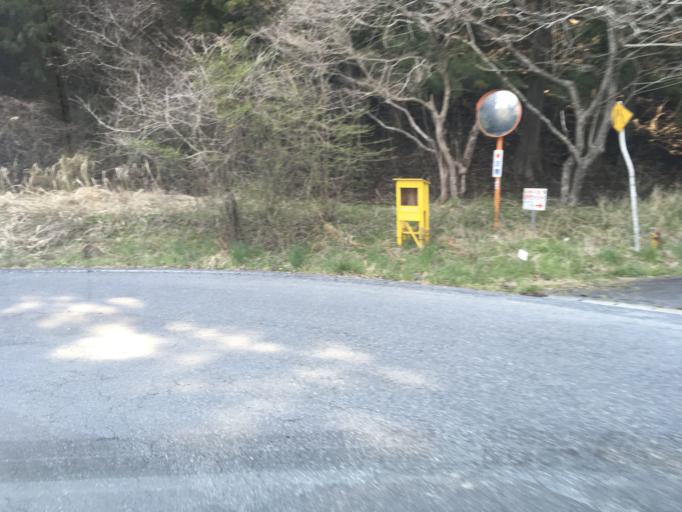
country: JP
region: Iwate
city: Ichinoseki
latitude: 38.8217
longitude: 141.3139
